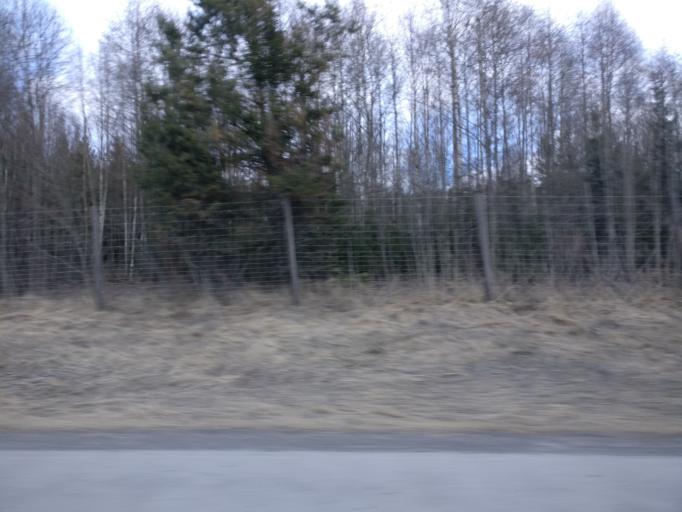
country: FI
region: Haeme
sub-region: Haemeenlinna
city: Janakkala
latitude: 60.8840
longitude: 24.5685
